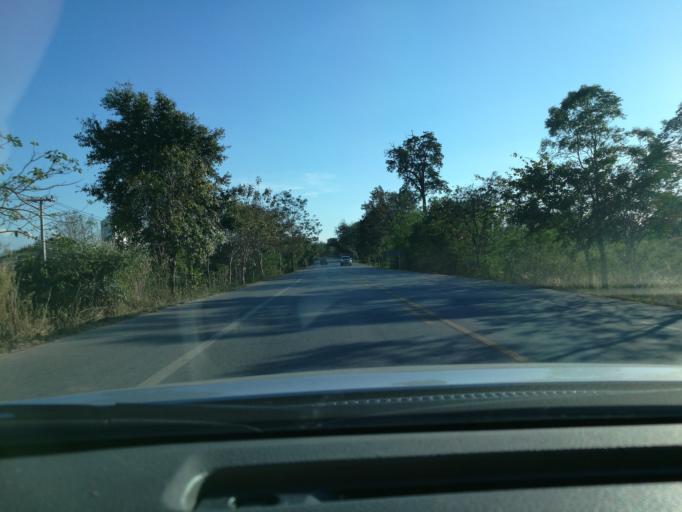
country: TH
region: Phitsanulok
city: Nakhon Thai
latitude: 17.0528
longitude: 100.8113
